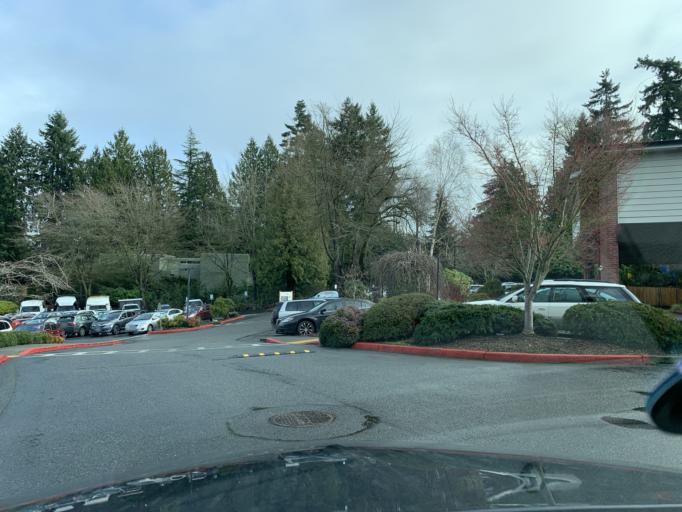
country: US
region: Washington
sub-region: King County
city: Mercer Island
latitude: 47.5812
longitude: -122.2151
